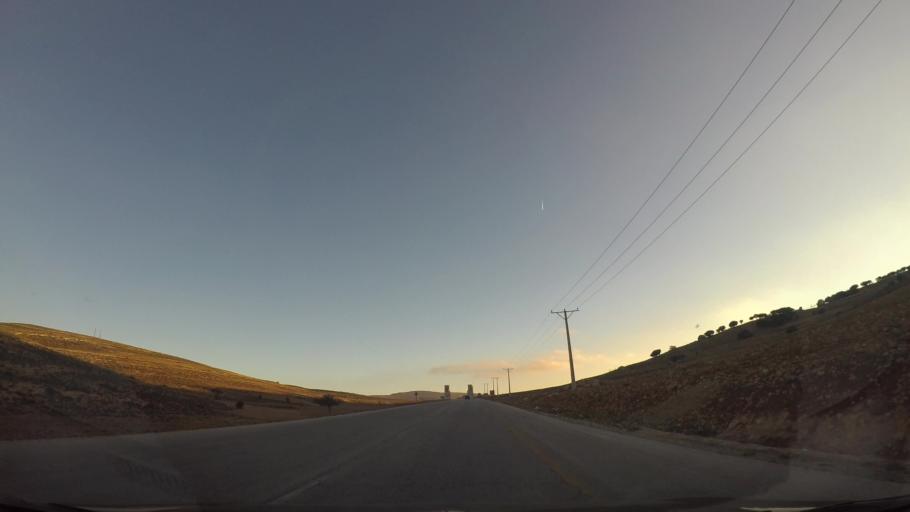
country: JO
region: Ma'an
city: Petra
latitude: 30.4060
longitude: 35.5041
